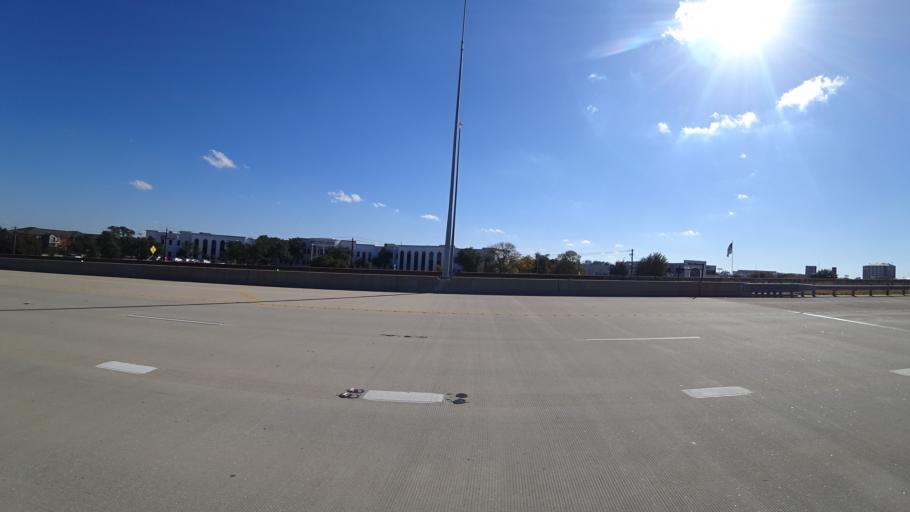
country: US
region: Texas
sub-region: Williamson County
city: Anderson Mill
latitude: 30.4716
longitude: -97.7878
